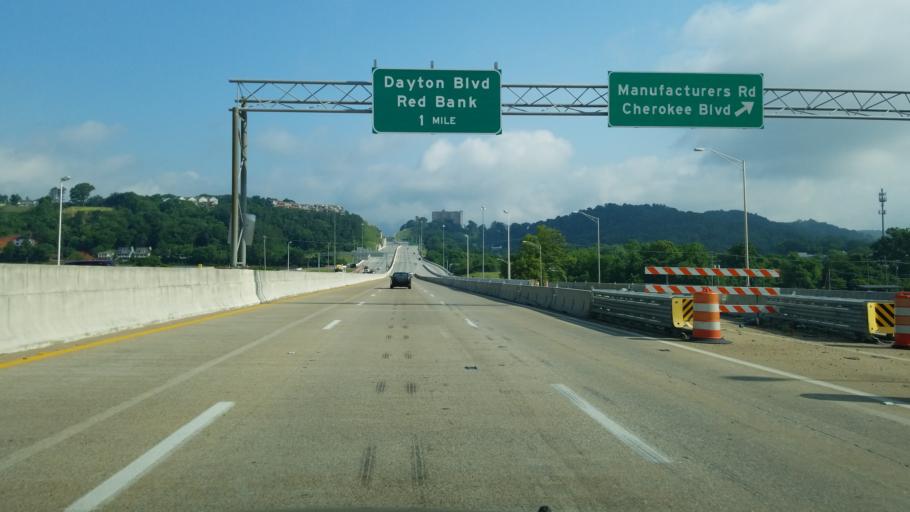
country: US
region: Tennessee
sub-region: Hamilton County
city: Chattanooga
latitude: 35.0595
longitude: -85.3167
